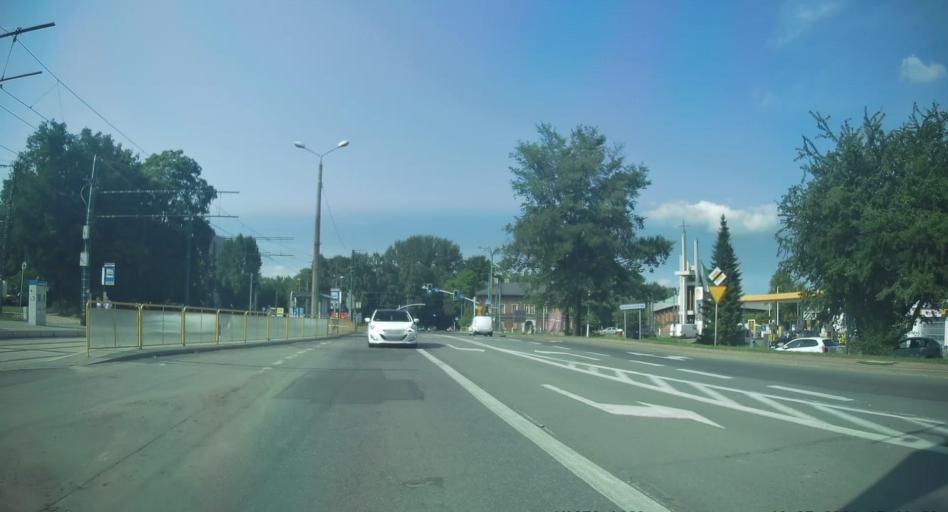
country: PL
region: Silesian Voivodeship
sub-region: Swietochlowice
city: Swietochlowice
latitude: 50.3042
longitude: 18.9192
